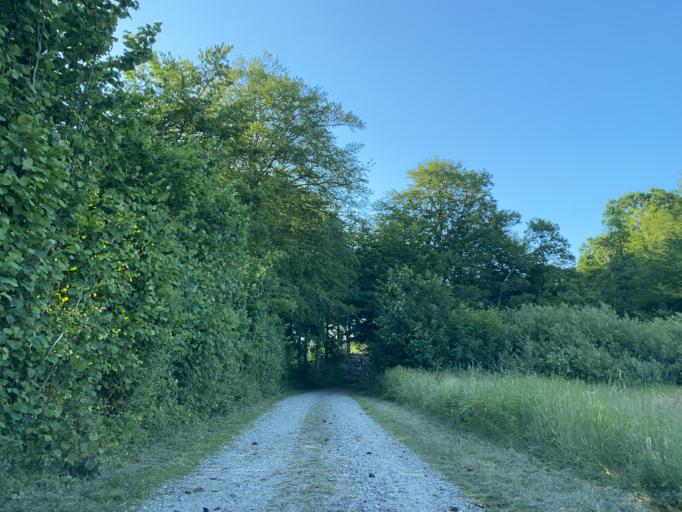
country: DK
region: South Denmark
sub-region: Haderslev Kommune
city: Starup
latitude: 55.1662
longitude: 9.5115
